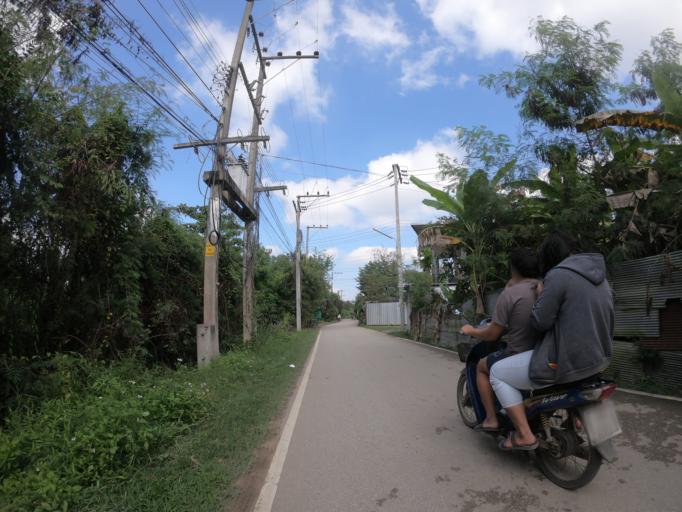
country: TH
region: Chiang Mai
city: Saraphi
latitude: 18.7188
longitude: 99.0158
